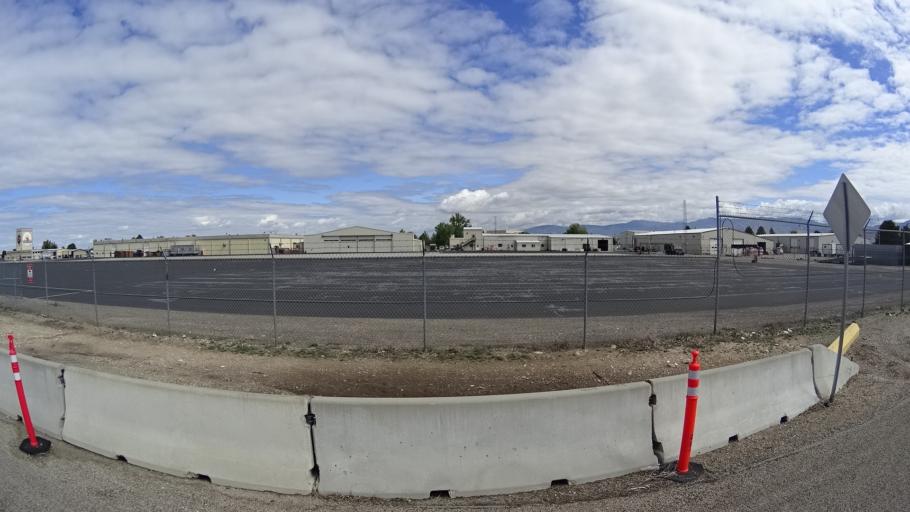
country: US
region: Idaho
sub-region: Ada County
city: Boise
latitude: 43.5643
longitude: -116.2094
